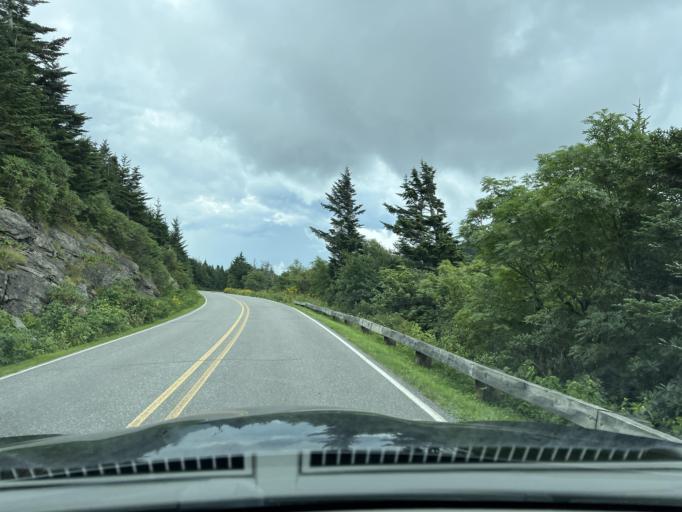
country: US
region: North Carolina
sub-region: Buncombe County
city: Black Mountain
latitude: 35.7482
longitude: -82.2777
